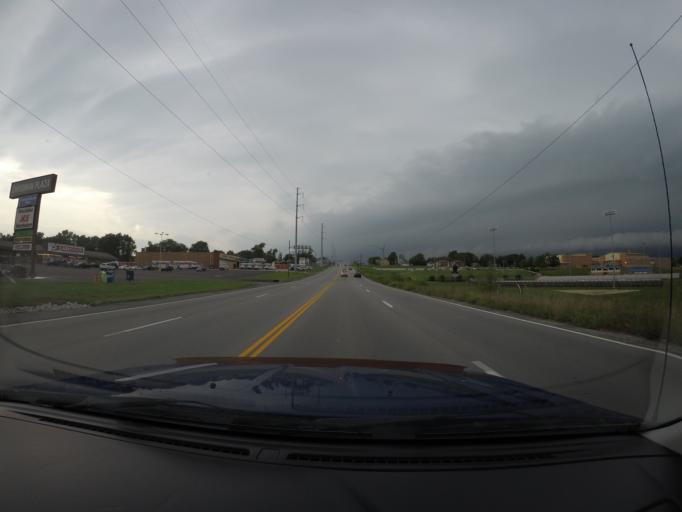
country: US
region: Missouri
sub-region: Jackson County
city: Independence
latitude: 39.1010
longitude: -94.4087
